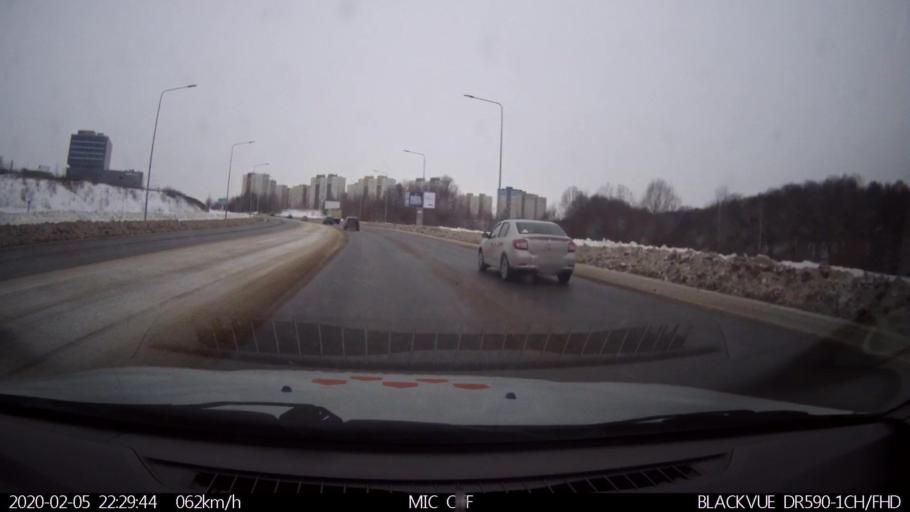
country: RU
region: Nizjnij Novgorod
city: Imeni Stepana Razina
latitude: 54.7472
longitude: 44.1483
